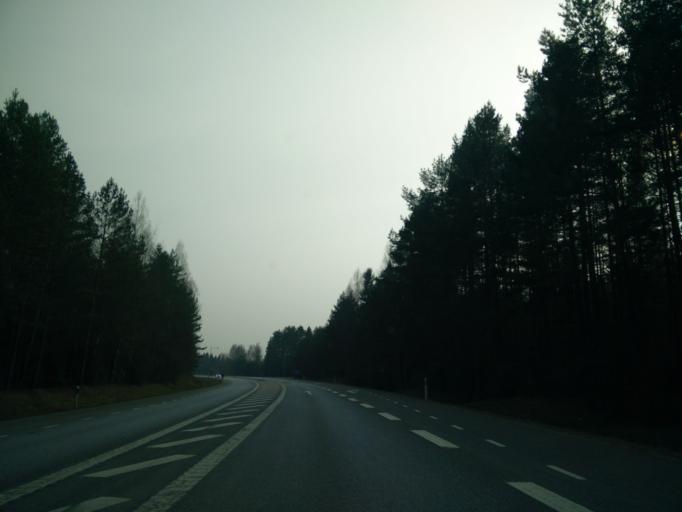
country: SE
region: Vaermland
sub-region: Forshaga Kommun
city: Forshaga
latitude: 59.4843
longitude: 13.4143
